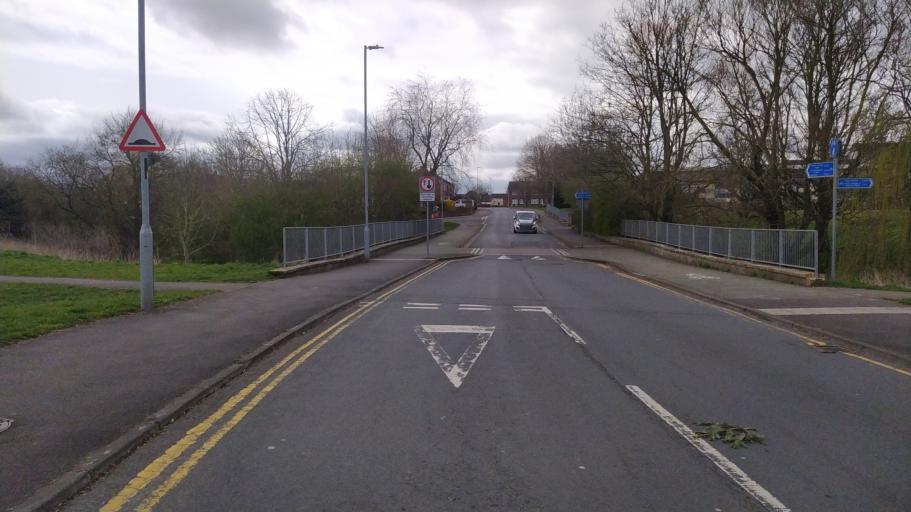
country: GB
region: England
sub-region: Wiltshire
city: Melksham
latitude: 51.3738
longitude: -2.1293
